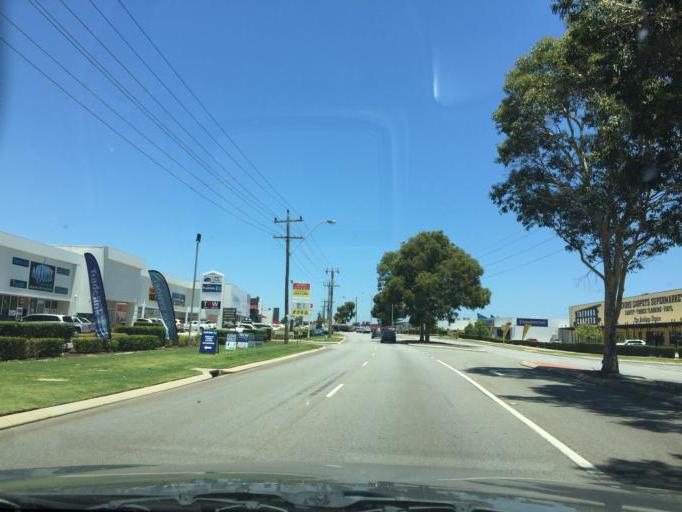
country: AU
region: Western Australia
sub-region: Canning
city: Canning Vale
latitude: -32.0592
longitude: 115.9090
